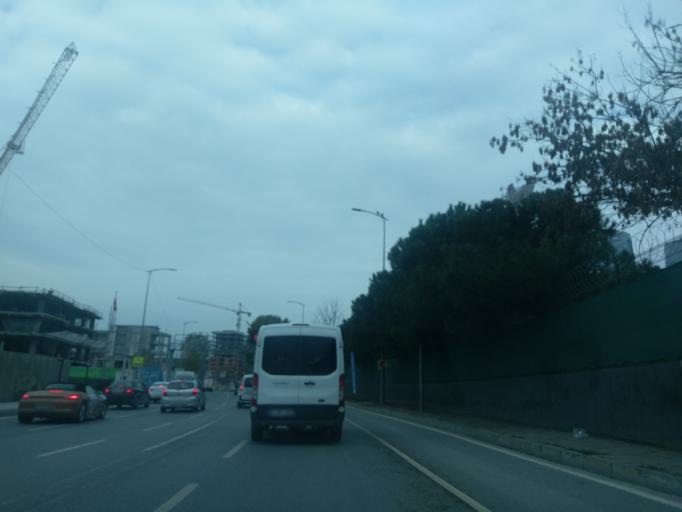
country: TR
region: Istanbul
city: Sisli
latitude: 41.0940
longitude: 28.9839
